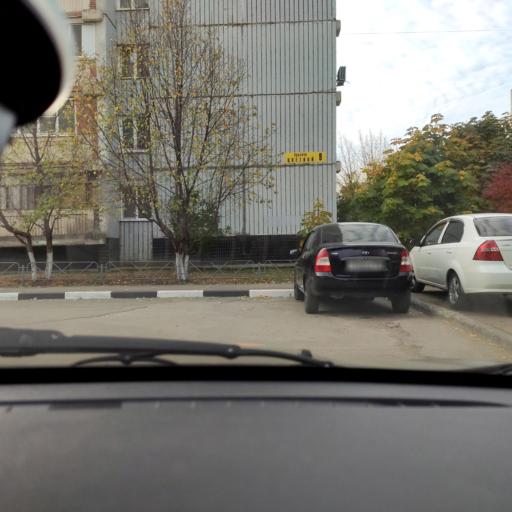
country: RU
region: Samara
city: Tol'yatti
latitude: 53.5395
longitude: 49.3392
